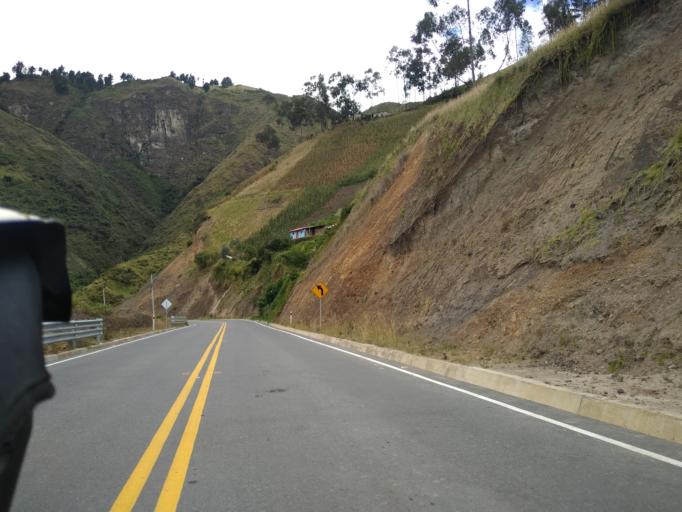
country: EC
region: Cotopaxi
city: Saquisili
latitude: -0.7561
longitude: -78.9127
